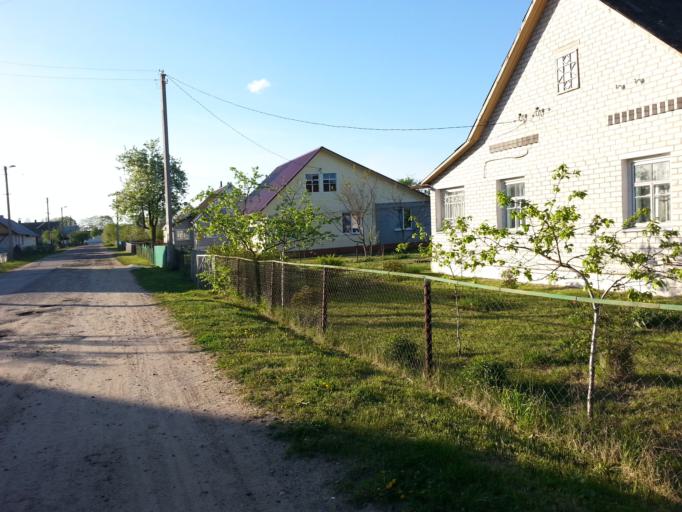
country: BY
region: Minsk
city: Narach
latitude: 54.9318
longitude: 26.6791
